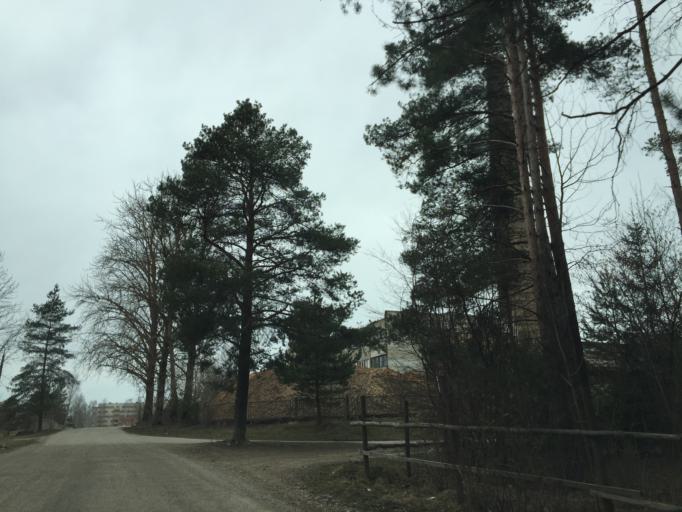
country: LV
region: Jekabpils Rajons
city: Jekabpils
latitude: 56.4897
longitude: 25.8960
